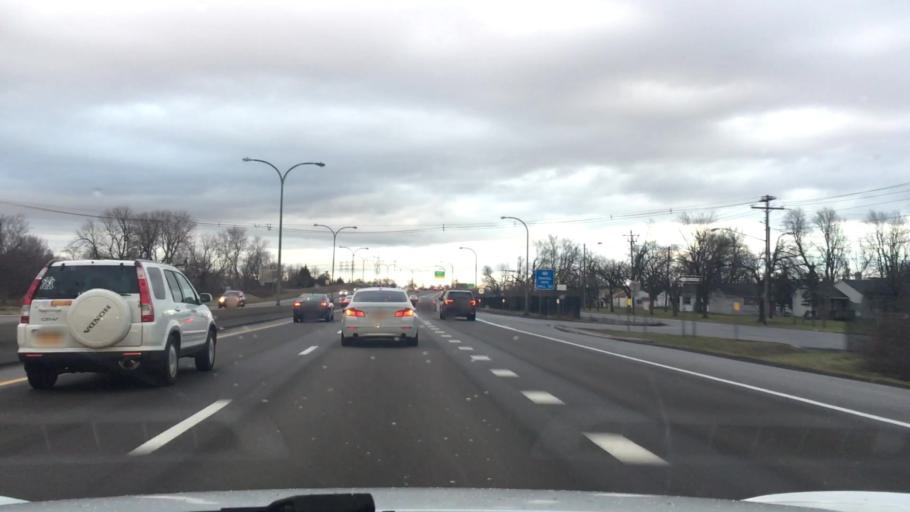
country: US
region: New York
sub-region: Erie County
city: Cheektowaga
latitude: 42.9330
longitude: -78.7779
